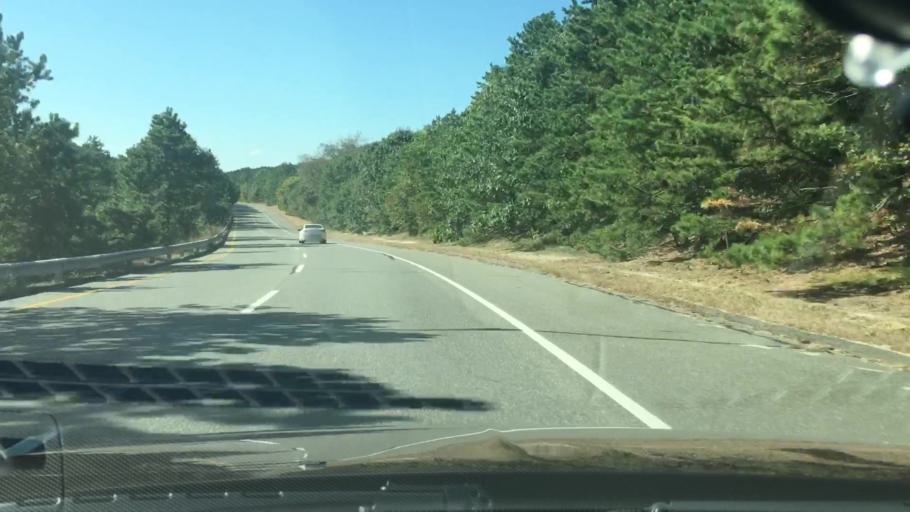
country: US
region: New York
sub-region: Suffolk County
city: North Patchogue
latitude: 40.7953
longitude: -73.0269
